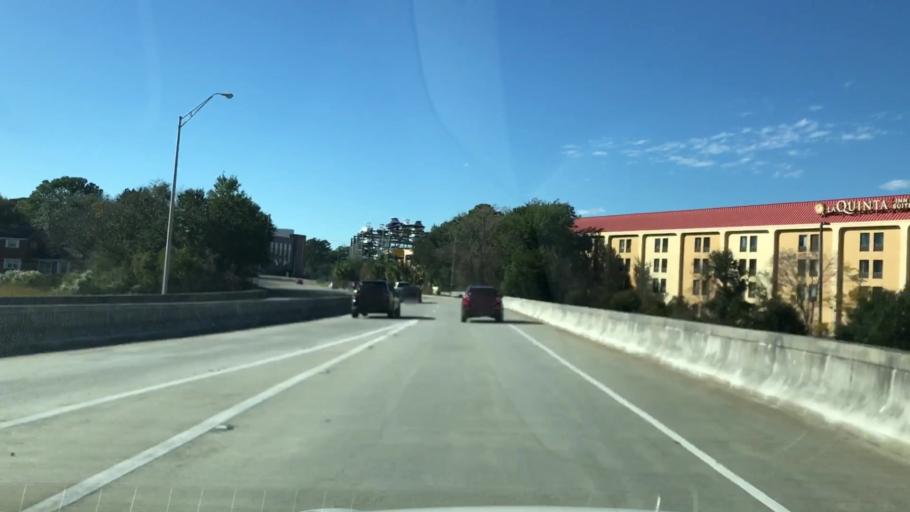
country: US
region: South Carolina
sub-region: Charleston County
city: Charleston
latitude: 32.7763
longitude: -79.9613
